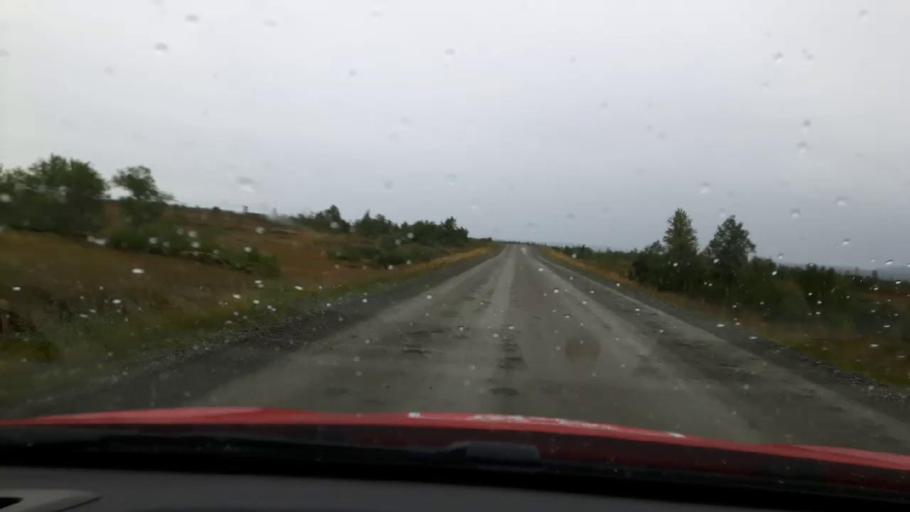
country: NO
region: Nord-Trondelag
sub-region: Meraker
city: Meraker
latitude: 63.6062
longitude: 12.2759
